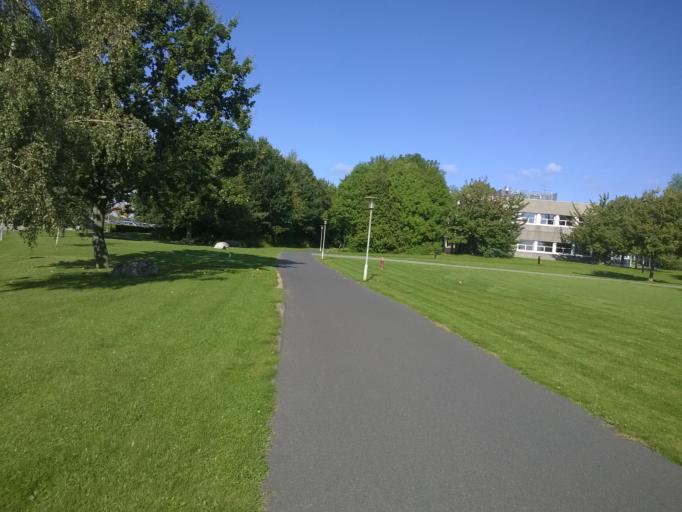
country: DK
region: Capital Region
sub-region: Ballerup Kommune
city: Ballerup
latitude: 55.7340
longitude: 12.3856
